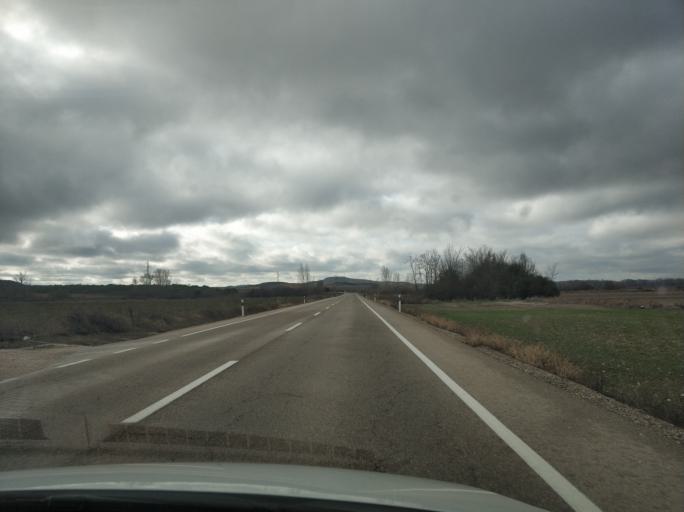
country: ES
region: Castille and Leon
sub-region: Provincia de Soria
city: San Esteban de Gormaz
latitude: 41.5673
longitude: -3.2328
